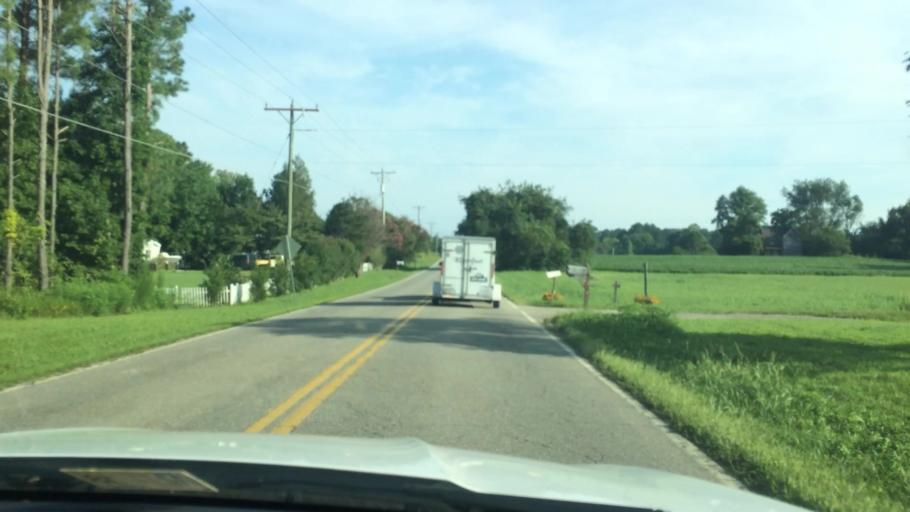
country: US
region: Virginia
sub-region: Middlesex County
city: Deltaville
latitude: 37.5683
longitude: -76.4532
